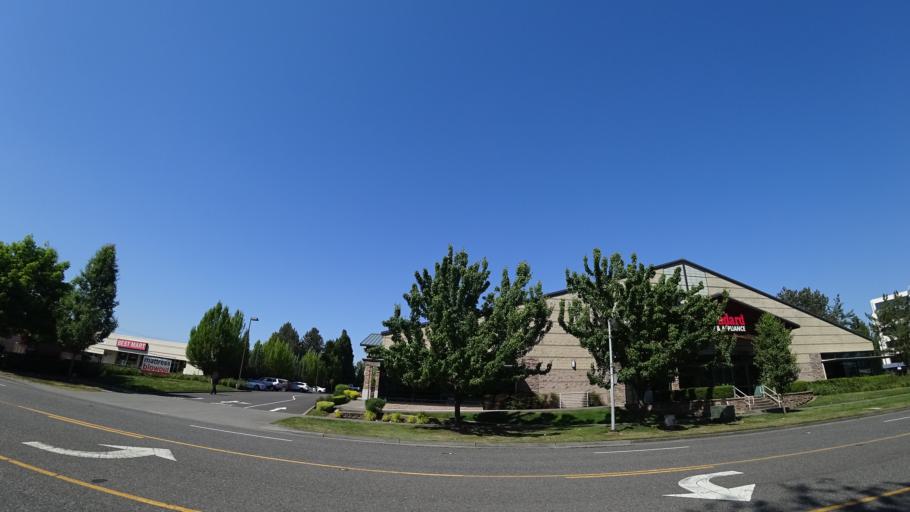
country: US
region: Oregon
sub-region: Washington County
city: Beaverton
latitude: 45.4938
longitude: -122.8087
